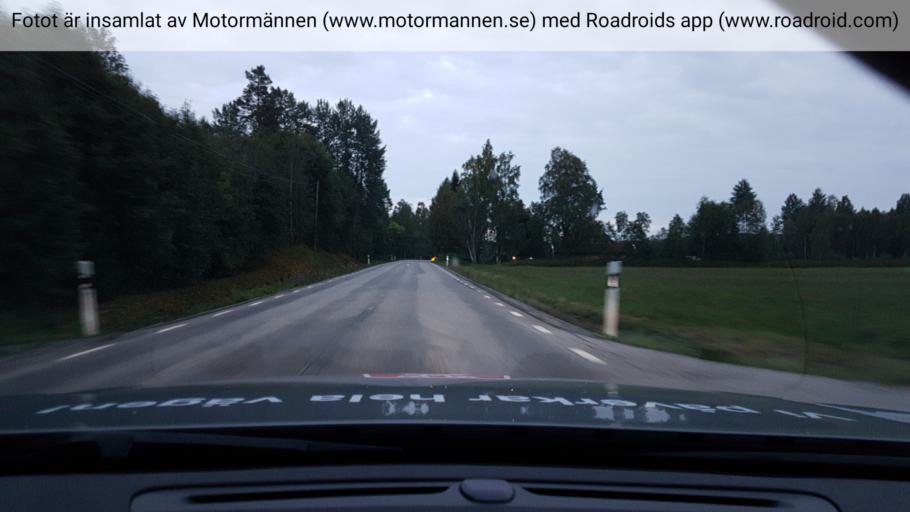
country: SE
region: OErebro
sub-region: Nora Kommun
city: As
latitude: 59.4673
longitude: 14.9040
